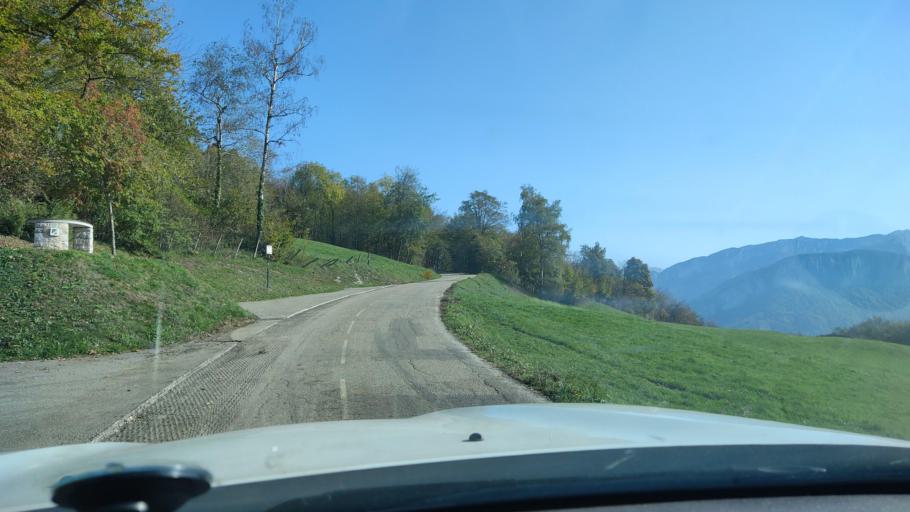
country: FR
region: Rhone-Alpes
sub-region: Departement de la Savoie
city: Les Echelles
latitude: 45.4628
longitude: 5.7668
